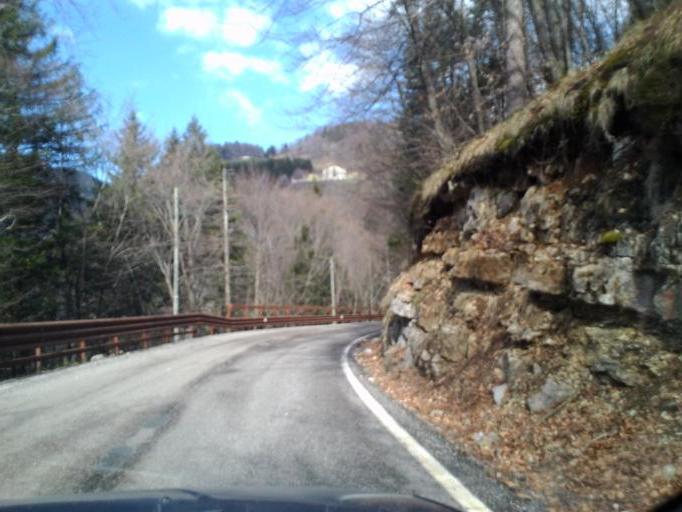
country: IT
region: Veneto
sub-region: Provincia di Verona
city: Erbezzo
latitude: 45.6524
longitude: 11.0177
